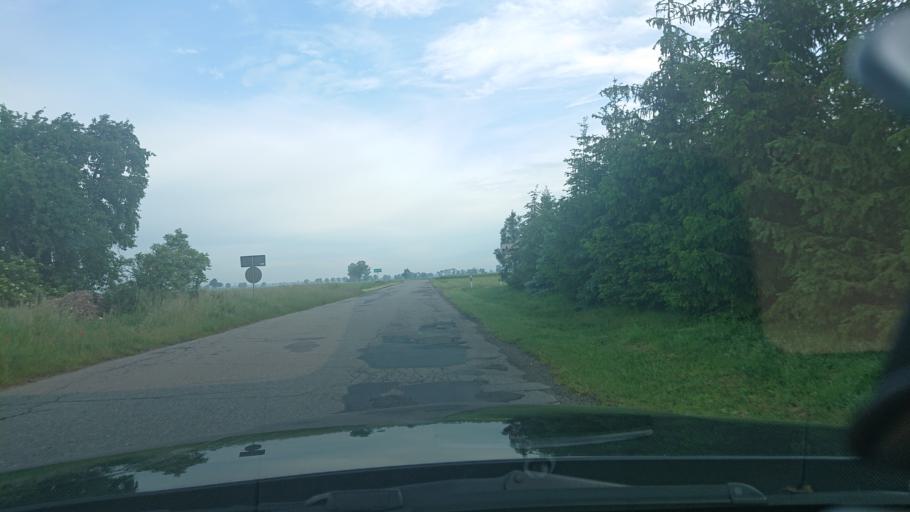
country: PL
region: Greater Poland Voivodeship
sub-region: Powiat gnieznienski
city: Mieleszyn
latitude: 52.6067
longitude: 17.5437
